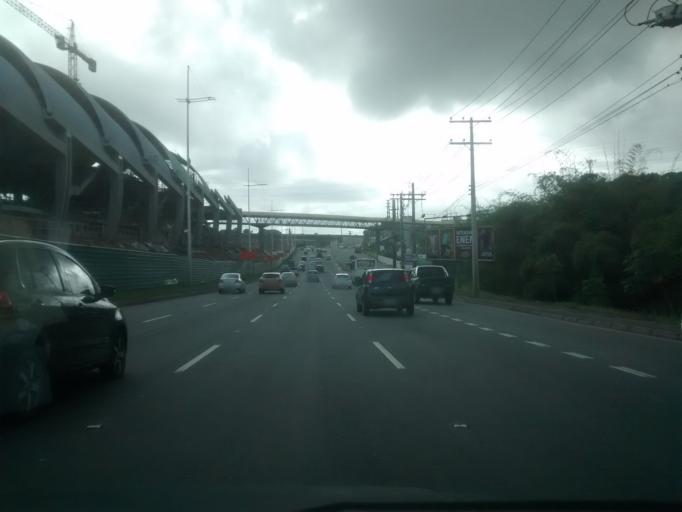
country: BR
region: Bahia
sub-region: Salvador
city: Salvador
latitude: -12.9465
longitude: -38.4217
